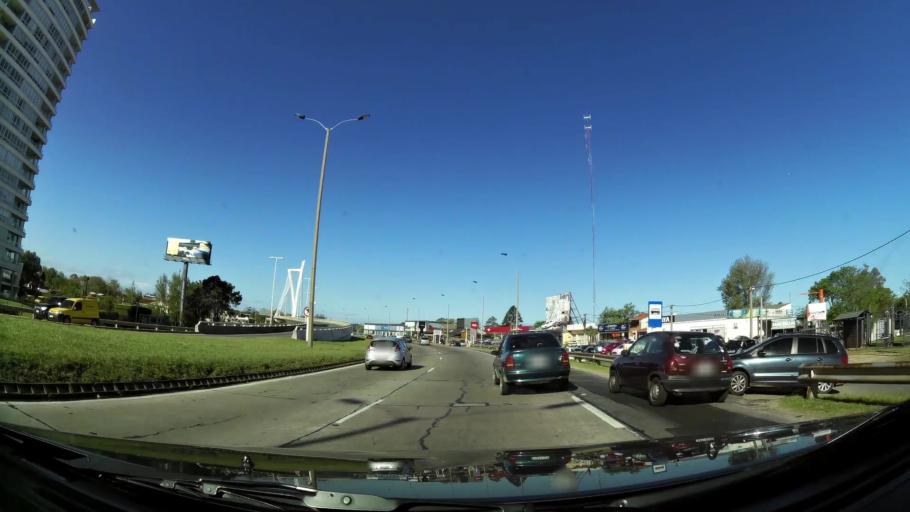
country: UY
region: Canelones
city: Barra de Carrasco
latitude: -34.8752
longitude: -56.0339
